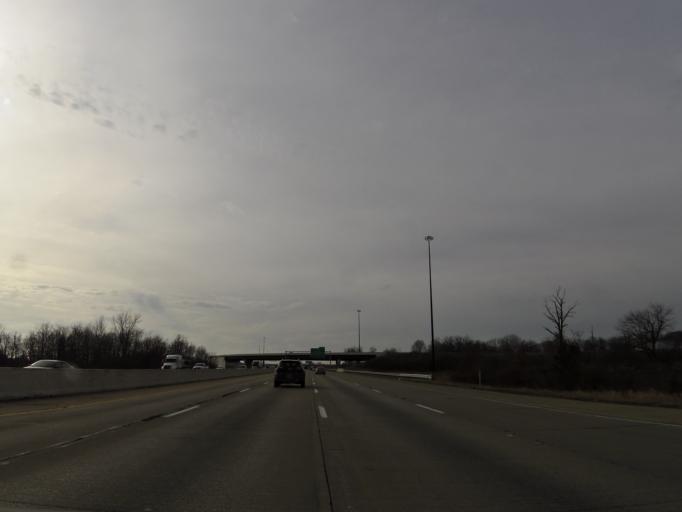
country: US
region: Indiana
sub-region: Marion County
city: Warren Park
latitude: 39.7476
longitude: -86.0365
